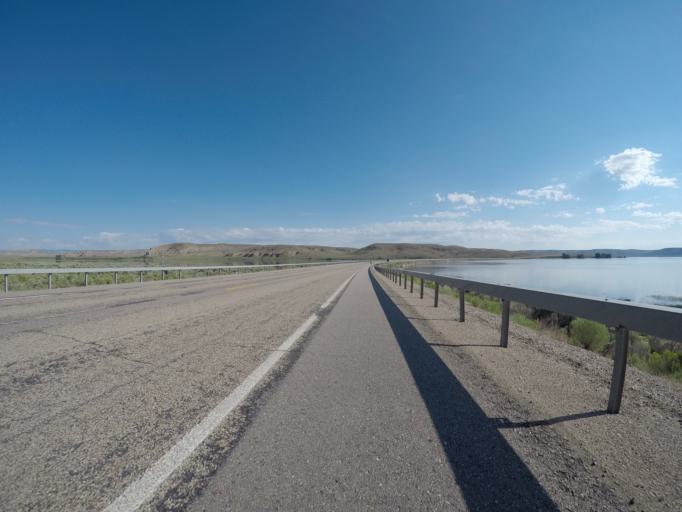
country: US
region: Wyoming
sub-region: Sublette County
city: Marbleton
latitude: 42.0816
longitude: -110.1603
